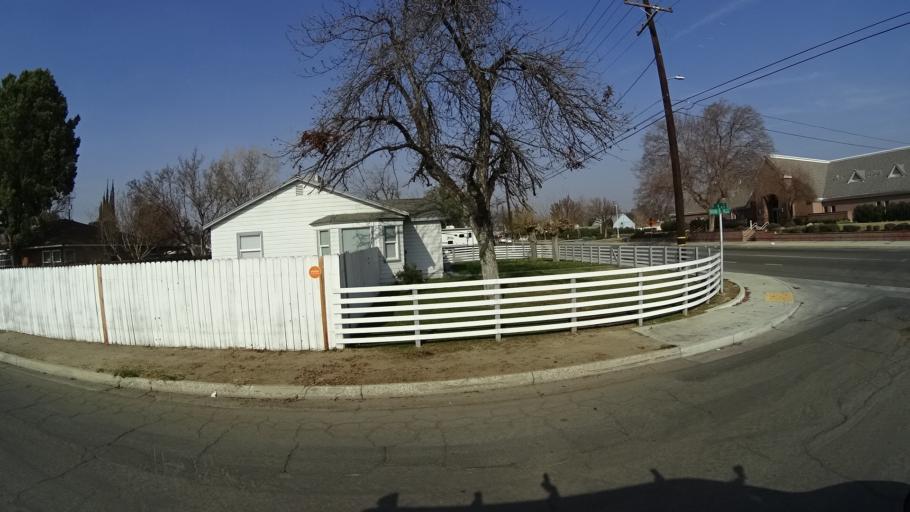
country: US
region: California
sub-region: Kern County
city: Bakersfield
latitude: 35.3599
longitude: -119.0297
